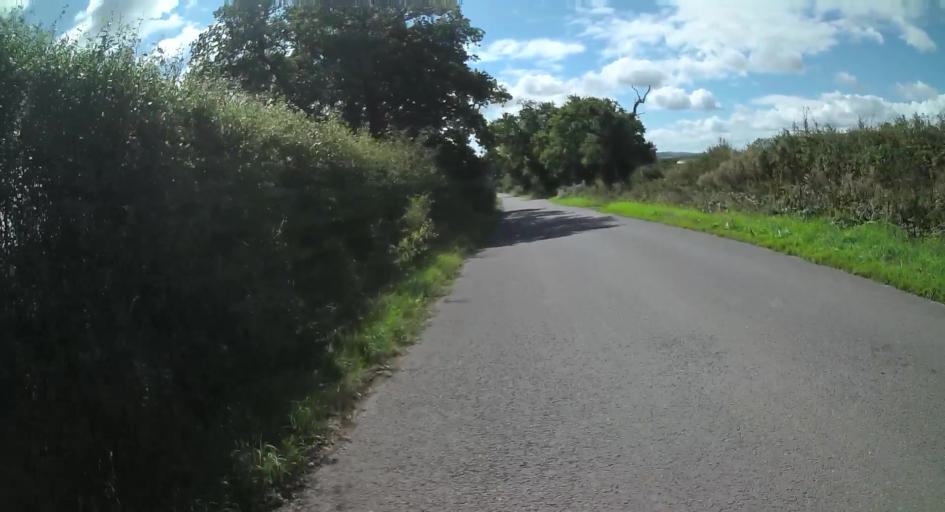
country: GB
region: England
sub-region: Isle of Wight
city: East Cowes
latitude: 50.7298
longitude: -1.2603
